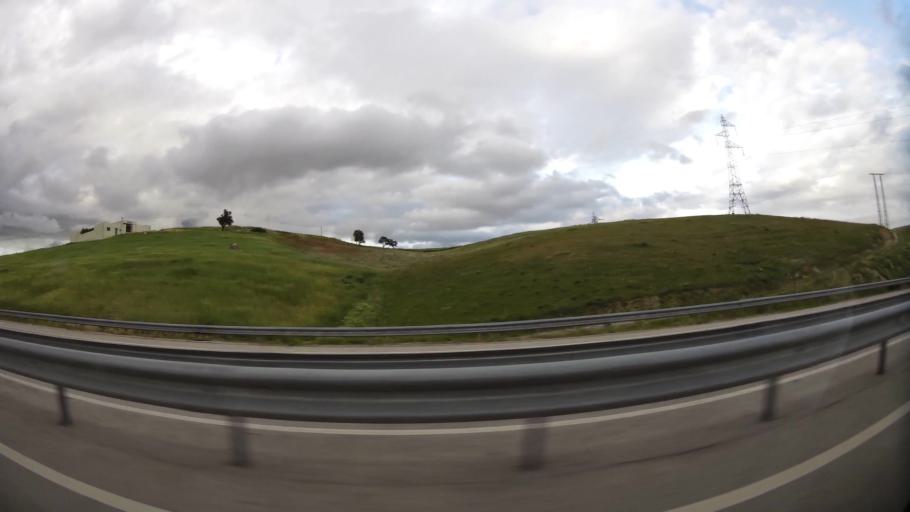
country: MA
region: Taza-Al Hoceima-Taounate
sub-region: Taza
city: Taza
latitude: 34.2623
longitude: -3.9559
